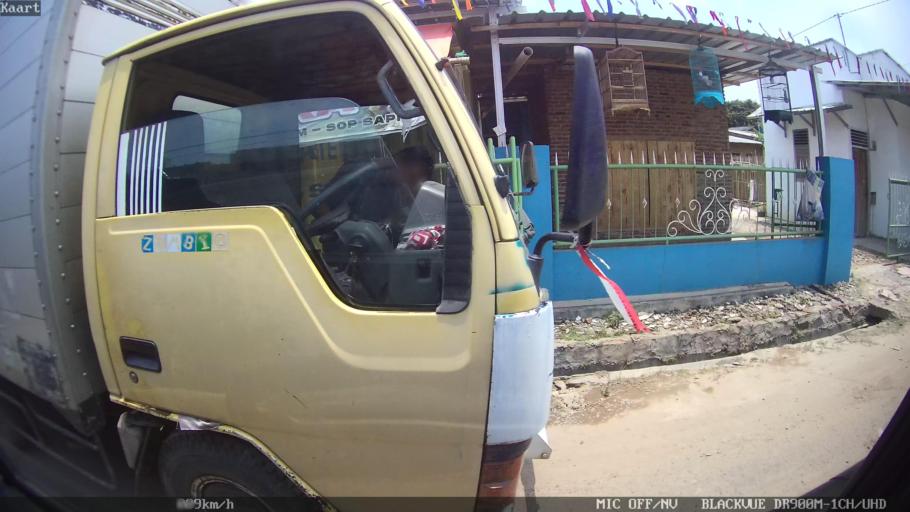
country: ID
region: Lampung
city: Kedaton
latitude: -5.3368
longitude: 105.2472
